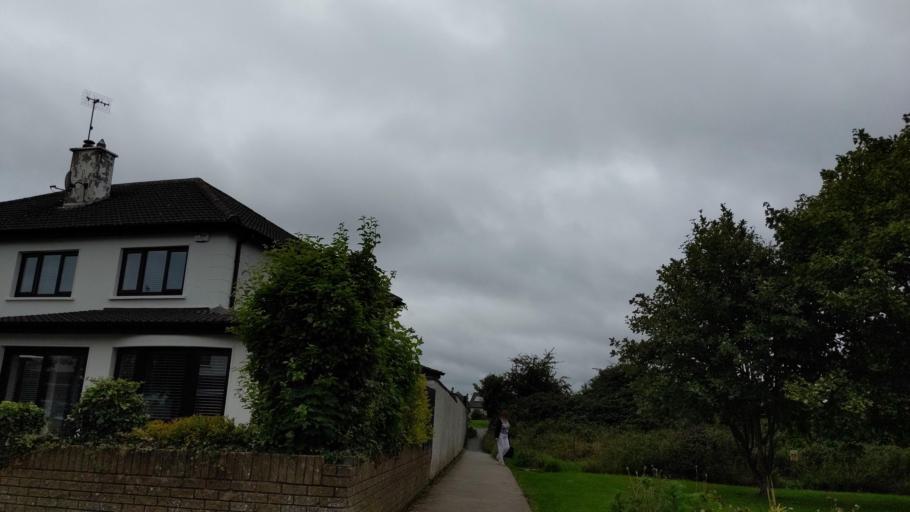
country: IE
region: Leinster
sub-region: Lu
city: Drogheda
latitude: 53.7047
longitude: -6.3502
